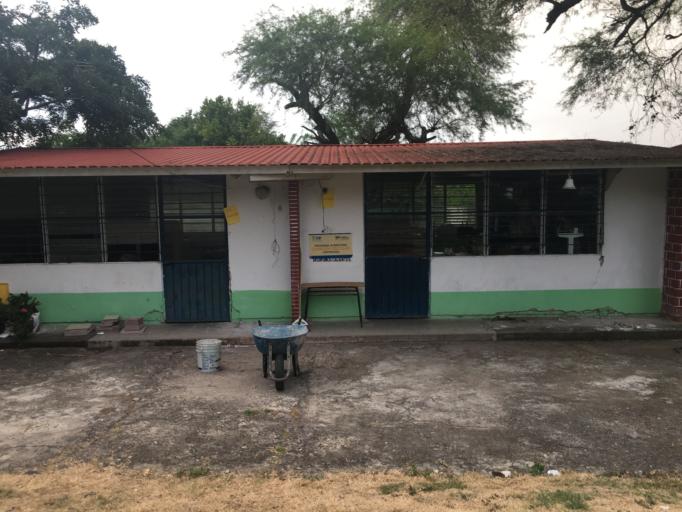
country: MX
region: Morelos
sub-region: Axochiapan
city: Quebrantadero
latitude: 18.5170
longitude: -98.8128
